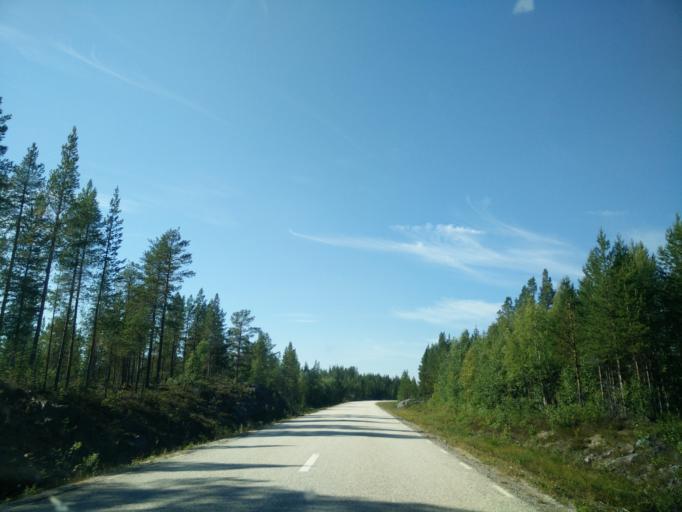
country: SE
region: Jaemtland
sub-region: Are Kommun
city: Jarpen
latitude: 62.8264
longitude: 13.4714
